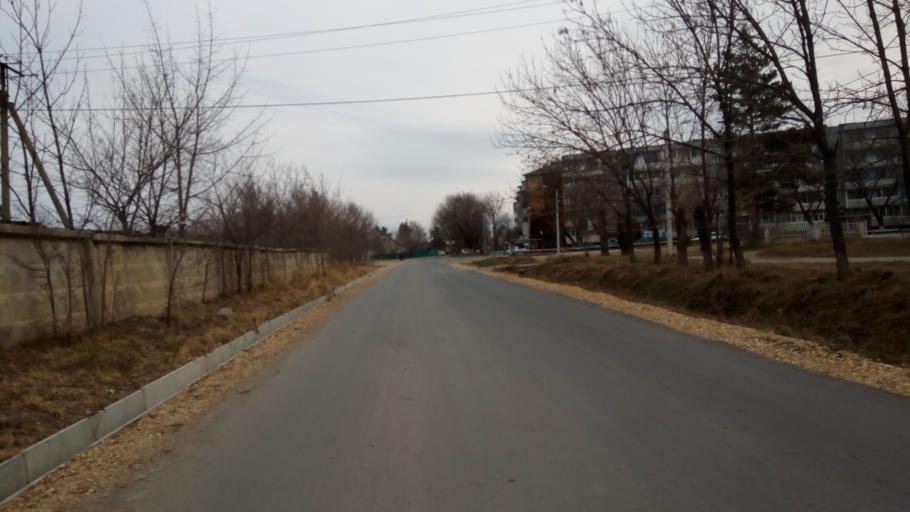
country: RU
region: Primorskiy
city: Novoshakhtinskiy
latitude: 44.0292
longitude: 132.1708
